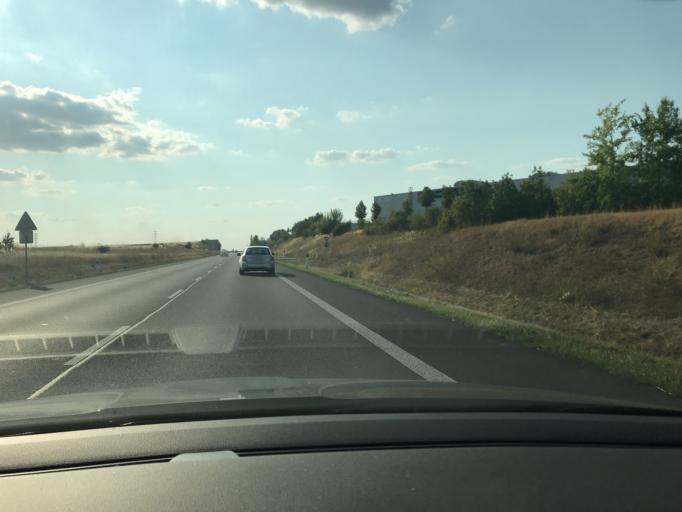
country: CZ
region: Ustecky
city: Cerncice
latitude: 50.3394
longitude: 13.8263
